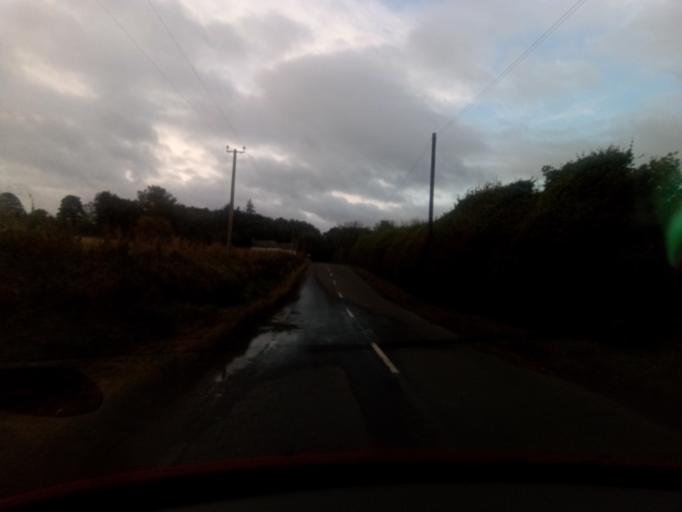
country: GB
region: Scotland
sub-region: The Scottish Borders
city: Jedburgh
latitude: 55.4241
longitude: -2.6157
